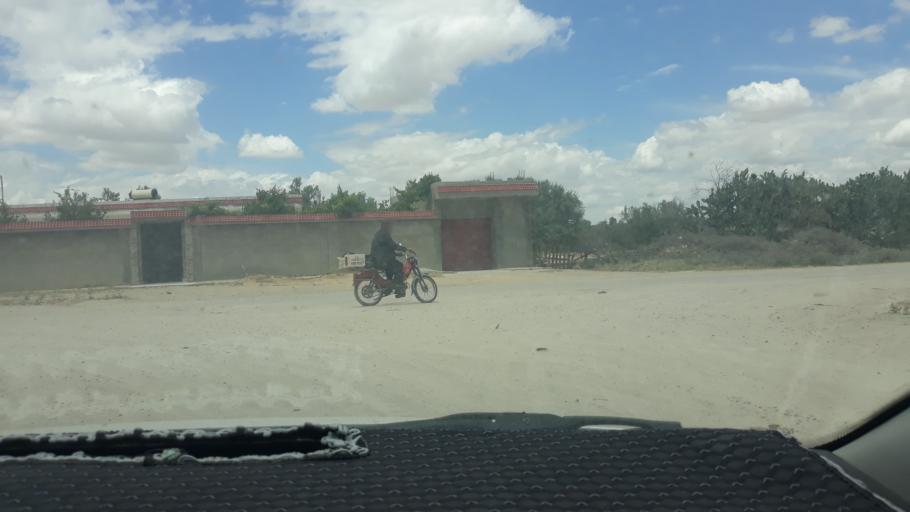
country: TN
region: Al Qayrawan
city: Kairouan
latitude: 35.6232
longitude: 9.9226
